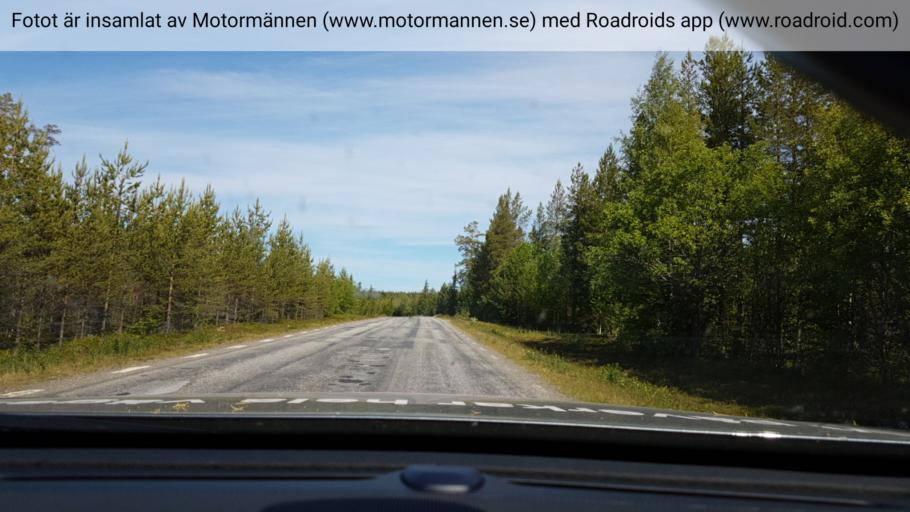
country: SE
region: Vaesterbotten
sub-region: Dorotea Kommun
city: Dorotea
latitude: 64.4040
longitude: 16.0563
